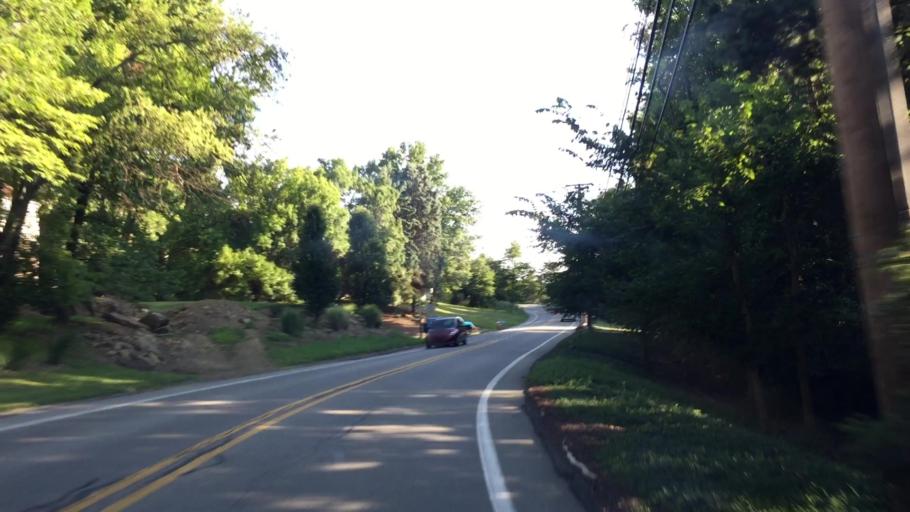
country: US
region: Pennsylvania
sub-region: Allegheny County
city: Franklin Park
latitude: 40.5688
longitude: -80.0774
